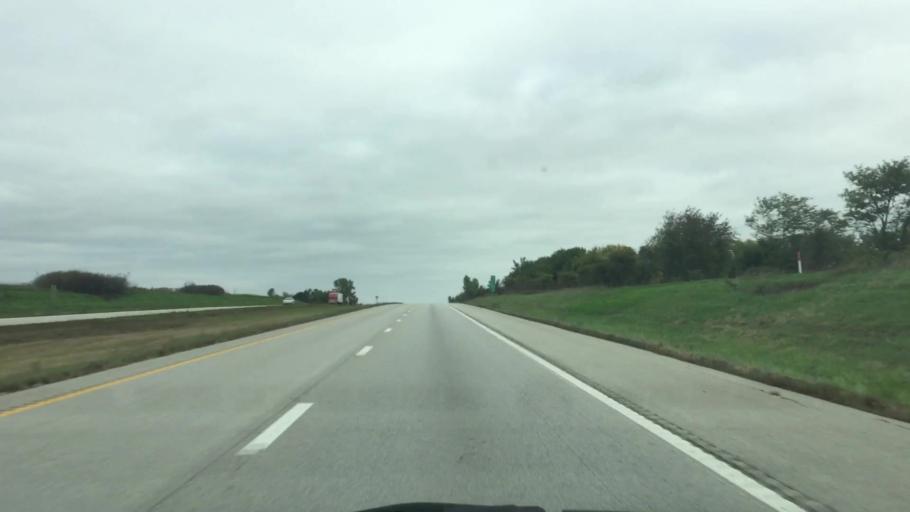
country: US
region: Missouri
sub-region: Clinton County
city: Cameron
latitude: 39.8078
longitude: -94.1969
